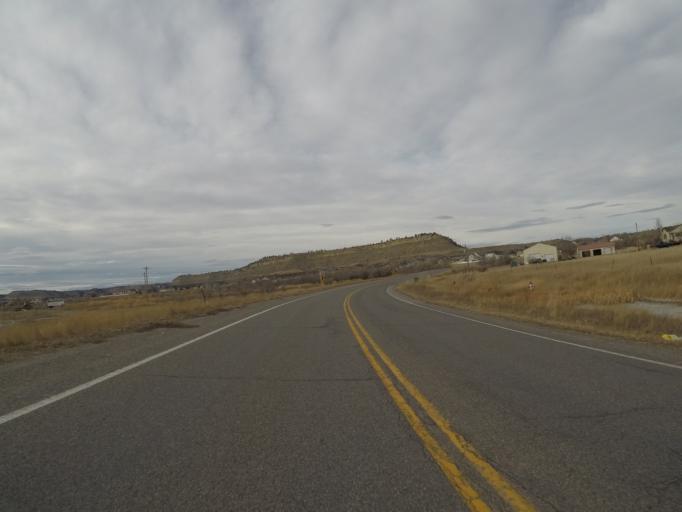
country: US
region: Montana
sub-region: Yellowstone County
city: Laurel
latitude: 45.7992
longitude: -108.6722
